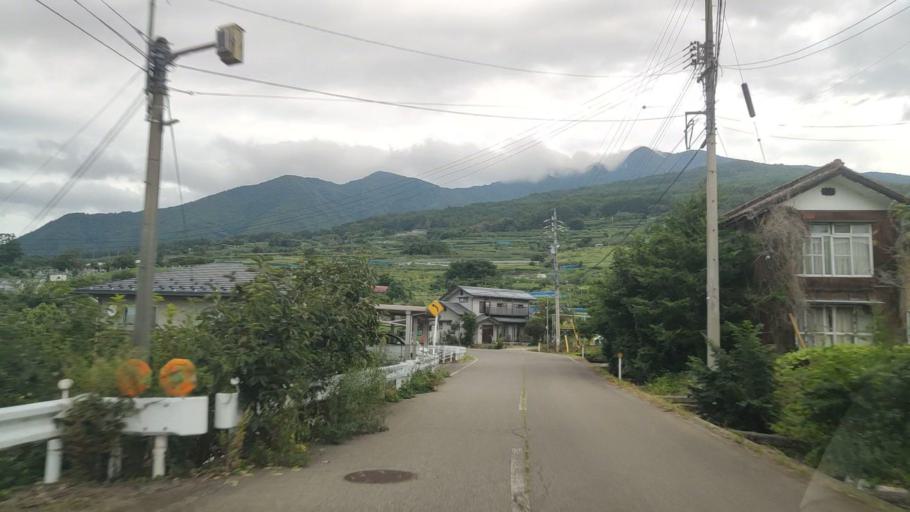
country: JP
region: Nagano
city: Nakano
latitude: 36.7777
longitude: 138.3753
